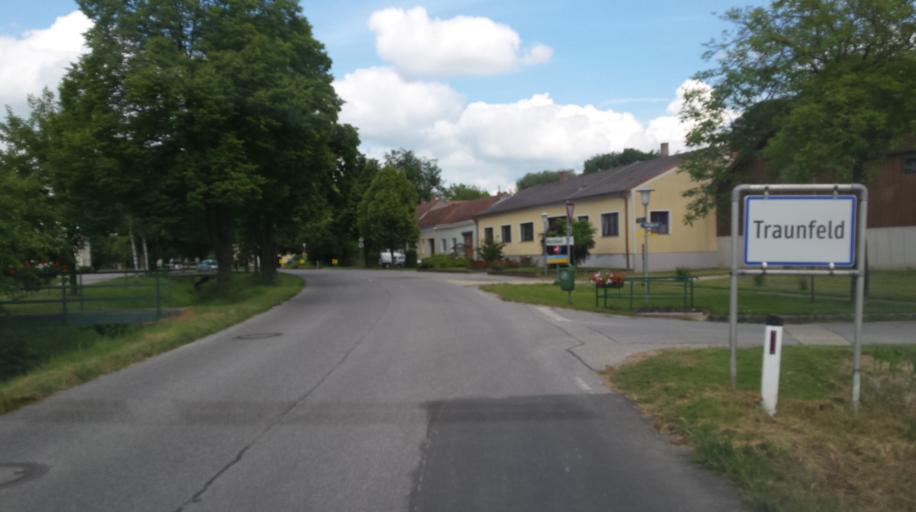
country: AT
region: Lower Austria
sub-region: Politischer Bezirk Mistelbach
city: Hochleithen
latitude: 48.4419
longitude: 16.5158
